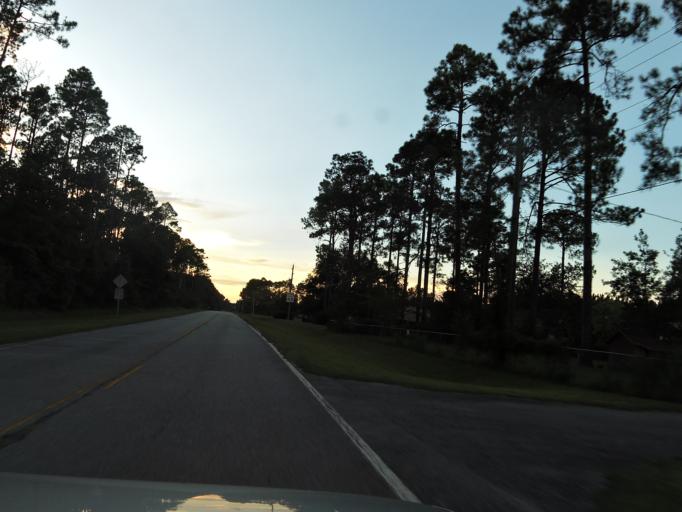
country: US
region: Georgia
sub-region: Camden County
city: Kingsland
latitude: 30.7654
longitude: -81.6892
